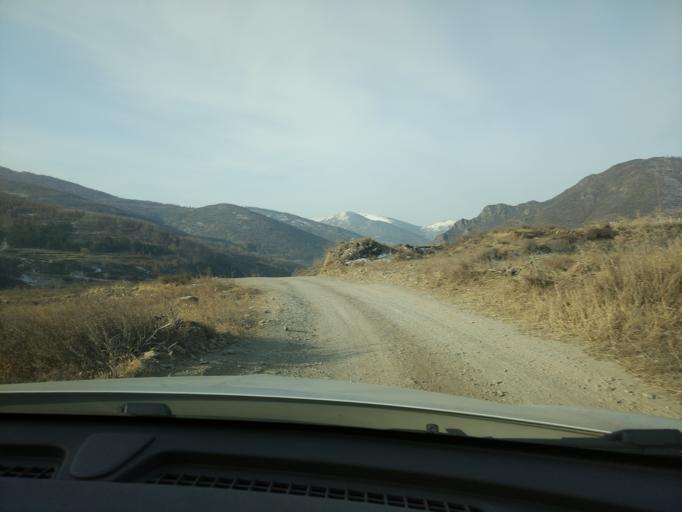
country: CN
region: Hebei
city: Xiwanzi
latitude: 40.8508
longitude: 115.4984
